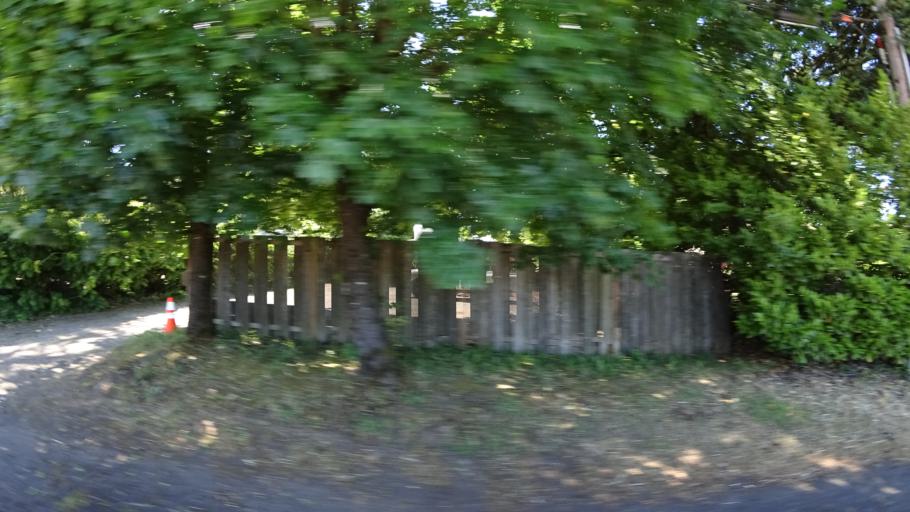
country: US
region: Oregon
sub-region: Multnomah County
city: Gresham
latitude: 45.4894
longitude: -122.4847
